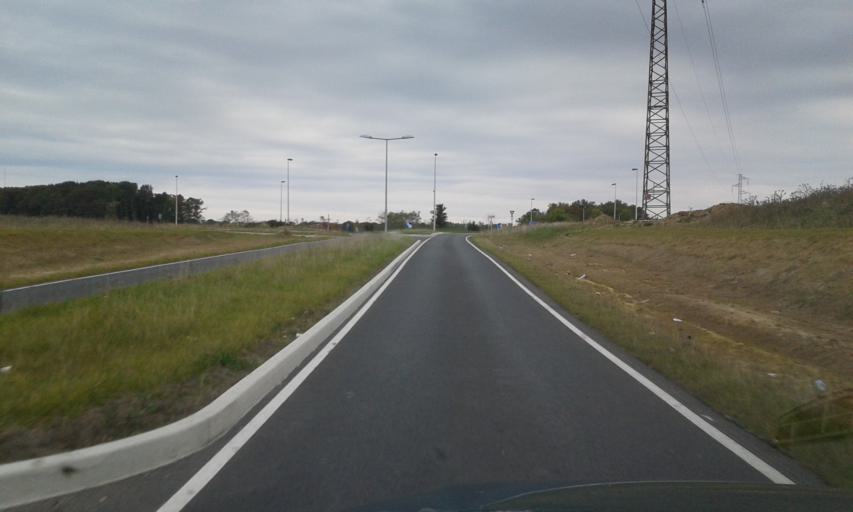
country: FR
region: Centre
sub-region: Departement du Loiret
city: Saran
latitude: 47.9611
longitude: 1.8820
